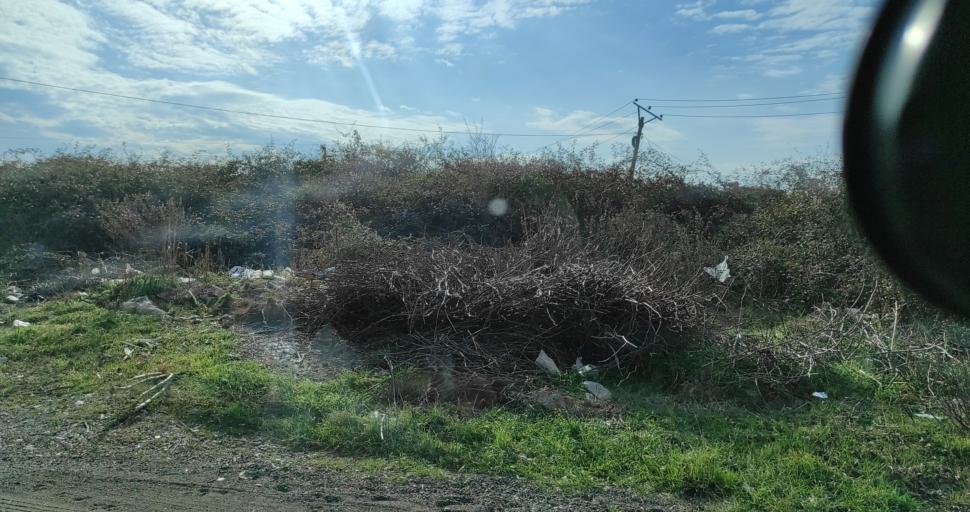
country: AL
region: Lezhe
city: Lezhe
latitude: 41.7891
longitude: 19.6265
